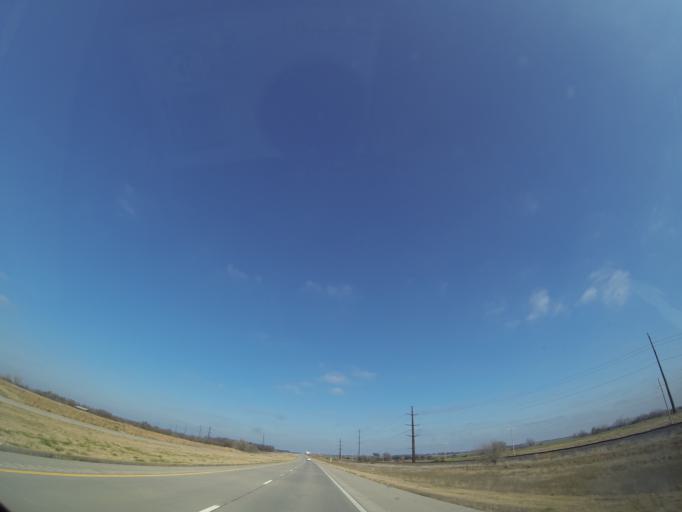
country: US
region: Kansas
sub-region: McPherson County
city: Inman
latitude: 38.1964
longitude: -97.8052
